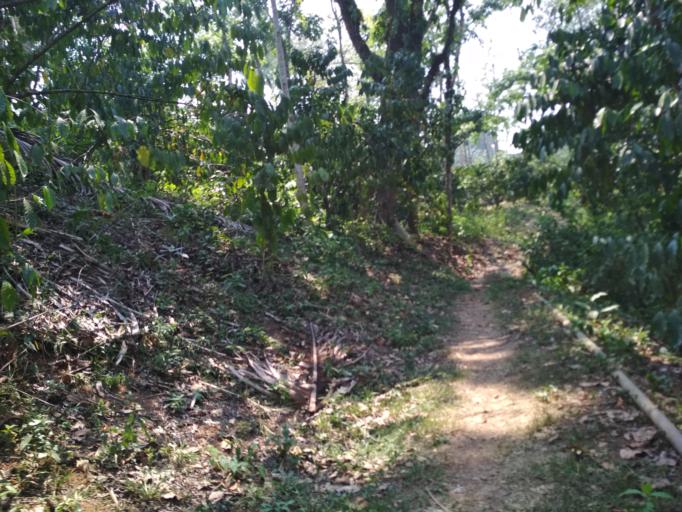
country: MX
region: Veracruz
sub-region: Tezonapa
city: Laguna Chica (Pueblo Nuevo)
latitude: 18.5561
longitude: -96.7275
